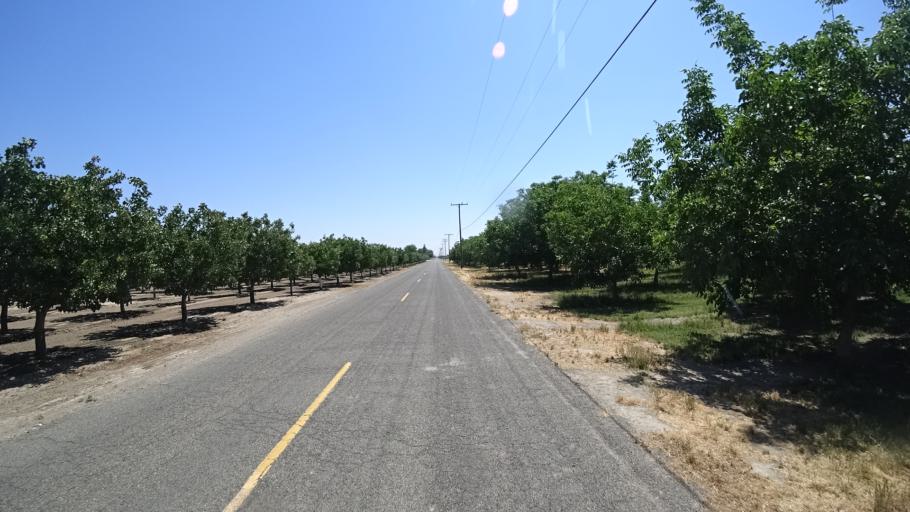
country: US
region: California
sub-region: Kings County
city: Armona
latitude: 36.3572
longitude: -119.7133
